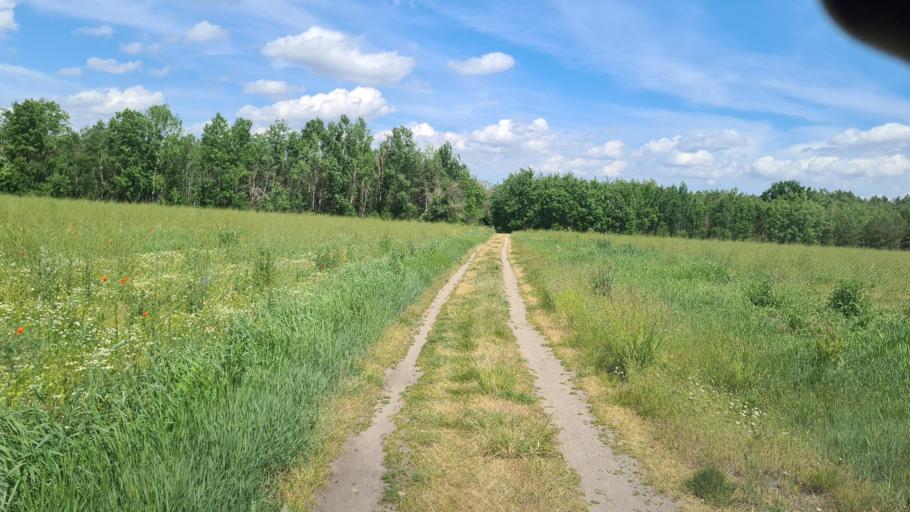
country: DE
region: Brandenburg
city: Sallgast
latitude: 51.5943
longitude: 13.8154
